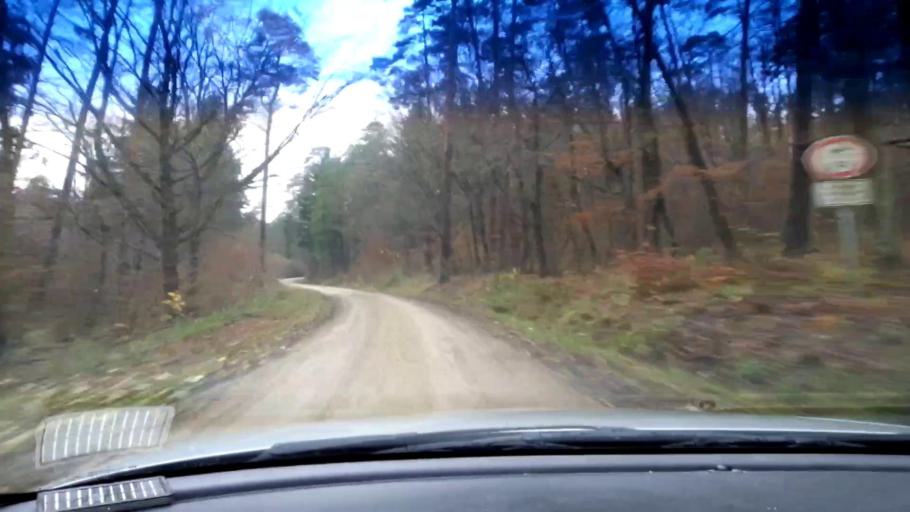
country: DE
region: Bavaria
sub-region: Upper Franconia
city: Memmelsdorf
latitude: 49.9423
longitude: 10.9449
